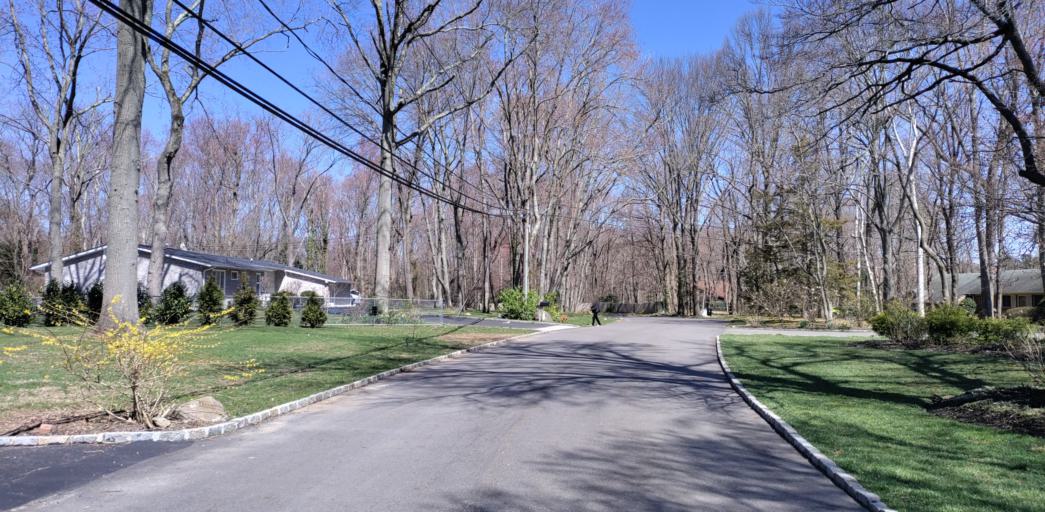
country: US
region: New York
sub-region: Nassau County
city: Greenvale
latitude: 40.8169
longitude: -73.6201
